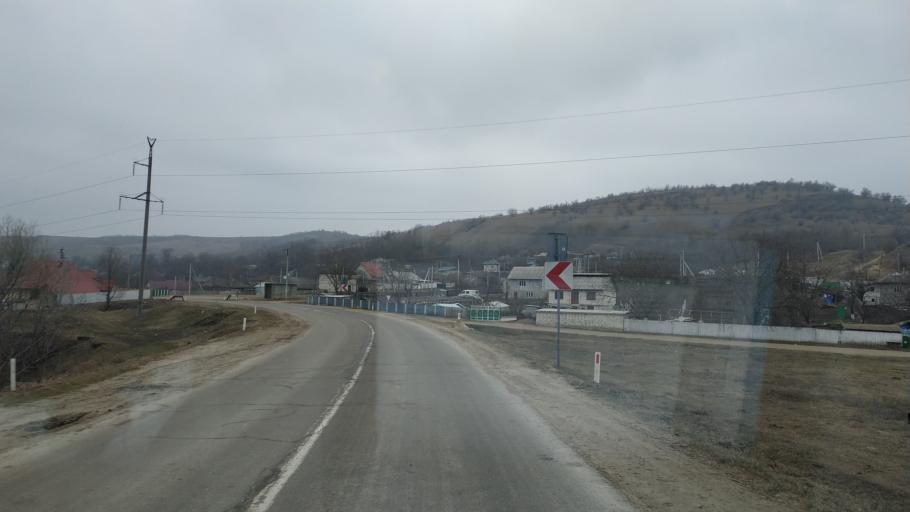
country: MD
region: Stinga Nistrului
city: Bucovat
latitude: 46.9889
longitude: 28.4425
